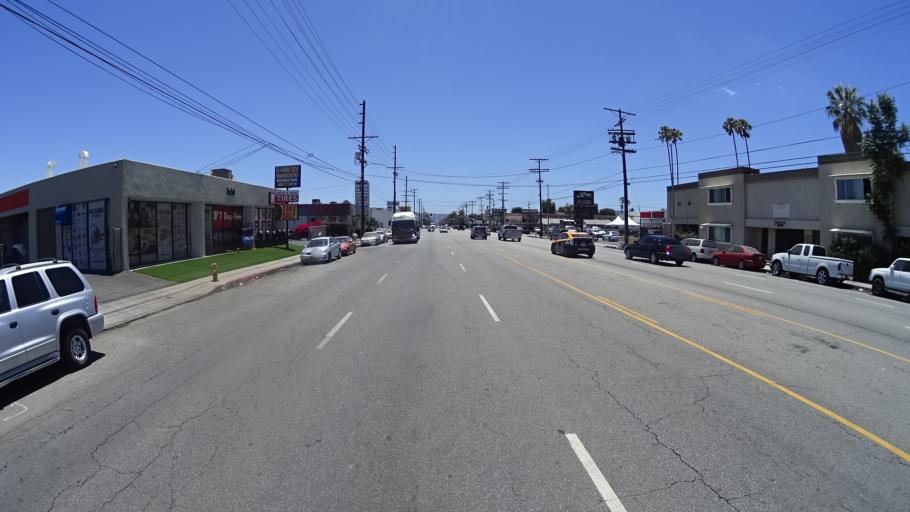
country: US
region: California
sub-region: Los Angeles County
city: Van Nuys
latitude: 34.2103
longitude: -118.4662
